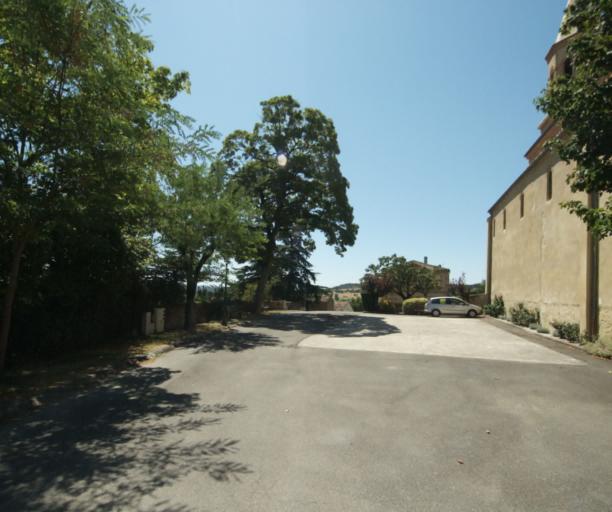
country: FR
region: Midi-Pyrenees
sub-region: Departement de la Haute-Garonne
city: Saint-Felix-Lauragais
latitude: 43.4789
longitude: 1.9250
